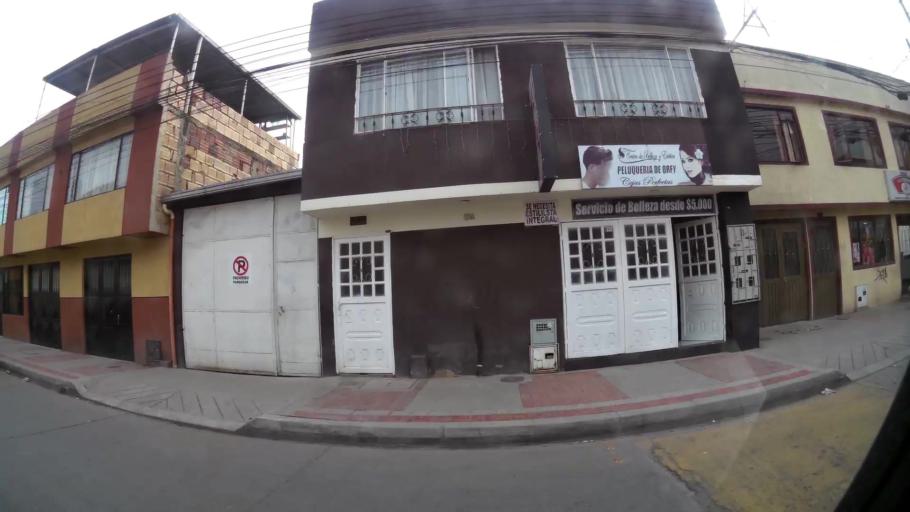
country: CO
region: Cundinamarca
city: Funza
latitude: 4.7071
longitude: -74.2118
